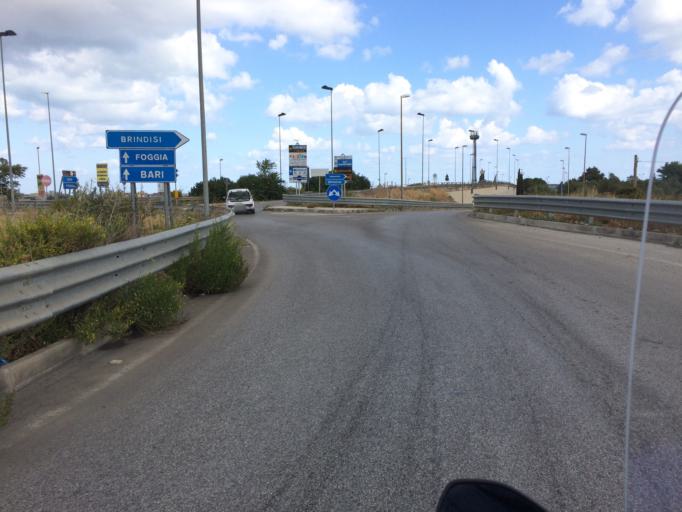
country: IT
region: Apulia
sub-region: Provincia di Bari
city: Modugno
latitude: 41.0940
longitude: 16.8281
